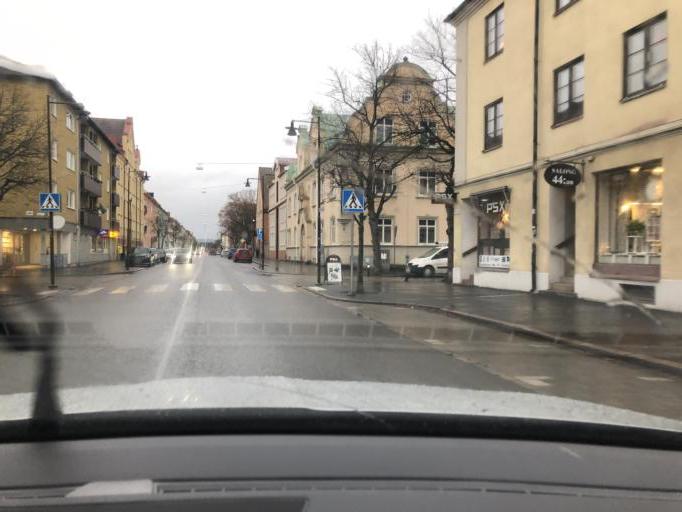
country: SE
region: Joenkoeping
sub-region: Jonkopings Kommun
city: Jonkoping
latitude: 57.7769
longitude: 14.1552
